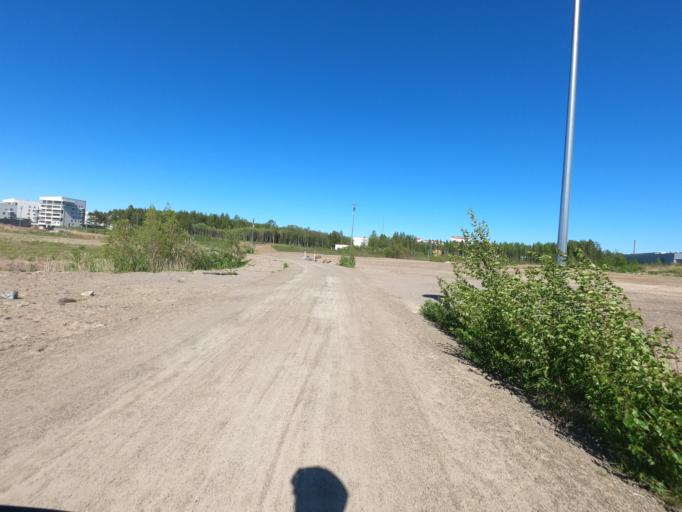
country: FI
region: North Karelia
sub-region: Joensuu
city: Joensuu
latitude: 62.5875
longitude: 29.7610
